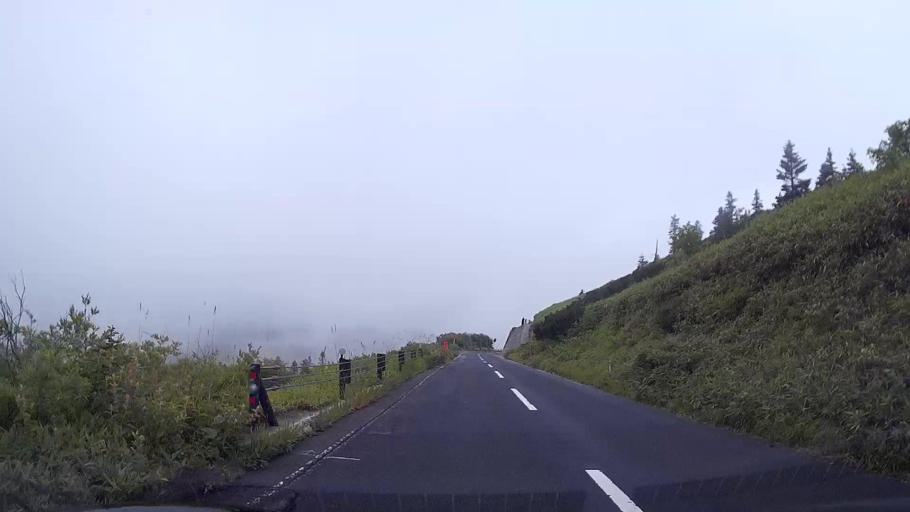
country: JP
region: Nagano
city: Nakano
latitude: 36.6565
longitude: 138.5297
